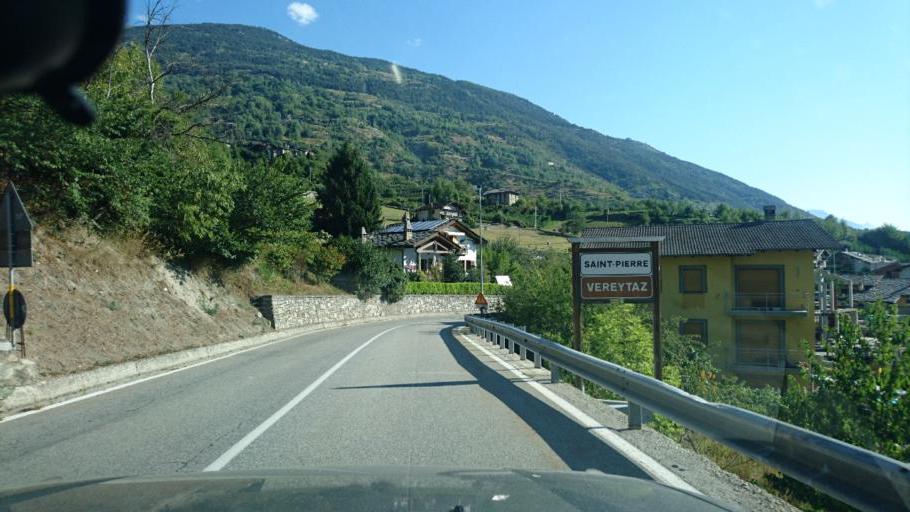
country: IT
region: Aosta Valley
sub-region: Valle d'Aosta
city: Saint-Pierre
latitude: 45.7122
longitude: 7.2145
